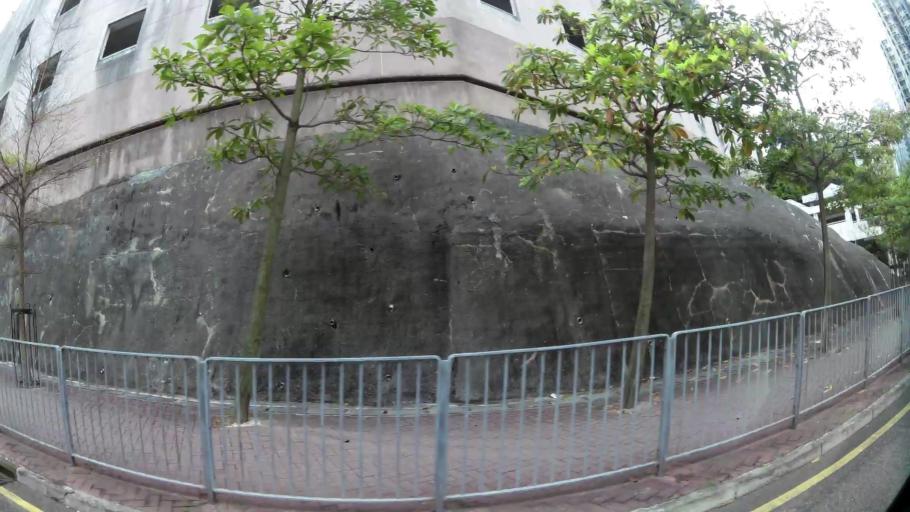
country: HK
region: Wanchai
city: Wan Chai
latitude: 22.2765
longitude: 114.2265
